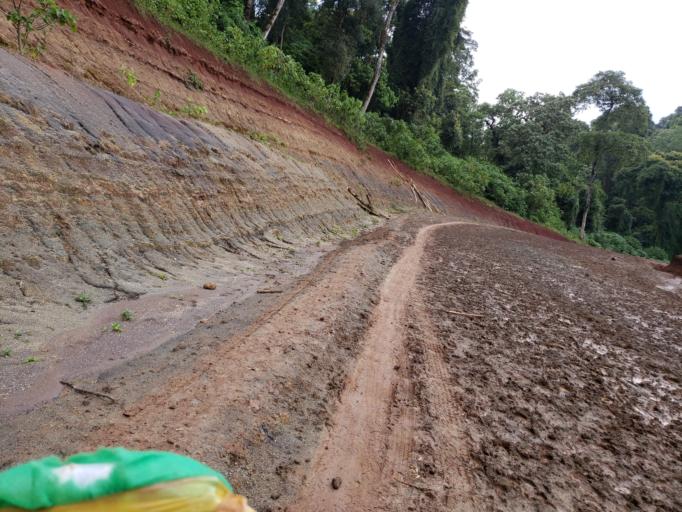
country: ET
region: Oromiya
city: Dodola
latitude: 6.4686
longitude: 39.5311
